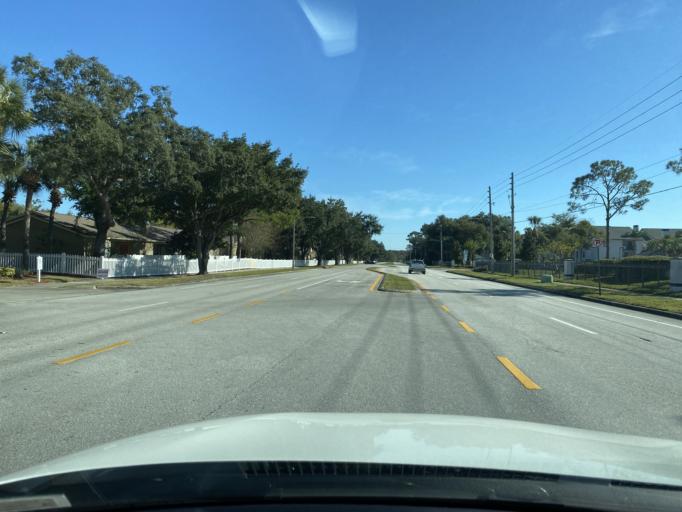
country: US
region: Florida
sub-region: Orange County
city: Azalea Park
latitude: 28.5171
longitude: -81.3083
